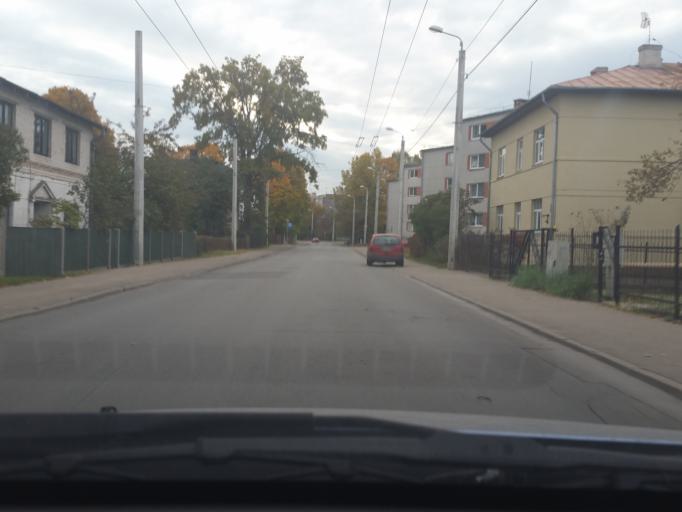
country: LV
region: Riga
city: Jaunciems
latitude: 56.9742
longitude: 24.1815
